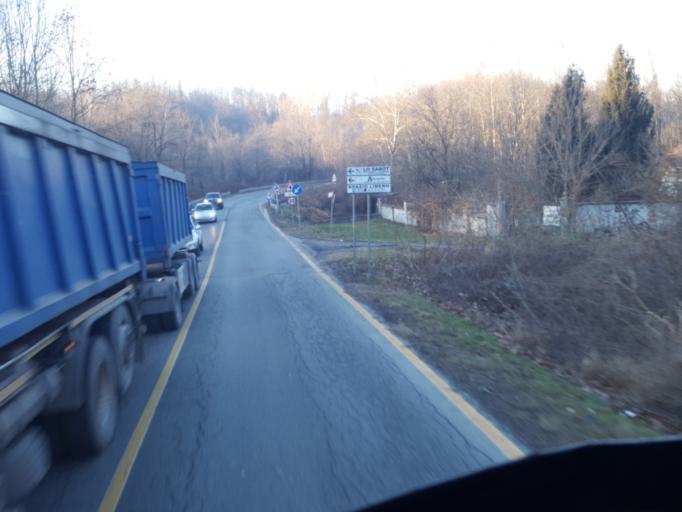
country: IT
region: Piedmont
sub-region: Provincia di Novara
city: Borgo Ticino
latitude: 45.7038
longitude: 8.5883
